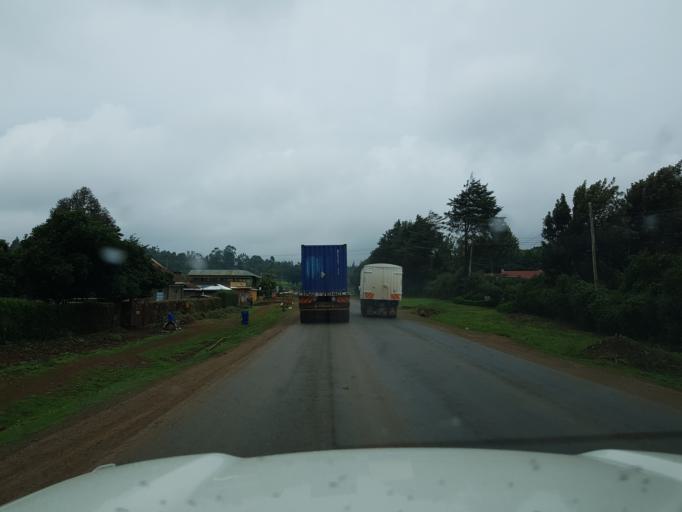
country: KE
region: Kiambu
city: Limuru
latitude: -1.1238
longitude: 36.6260
